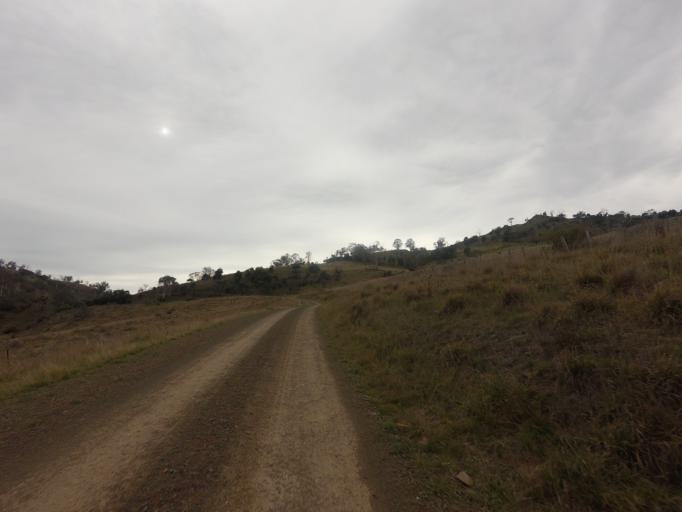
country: AU
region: Tasmania
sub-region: Derwent Valley
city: New Norfolk
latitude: -42.3646
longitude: 146.8425
